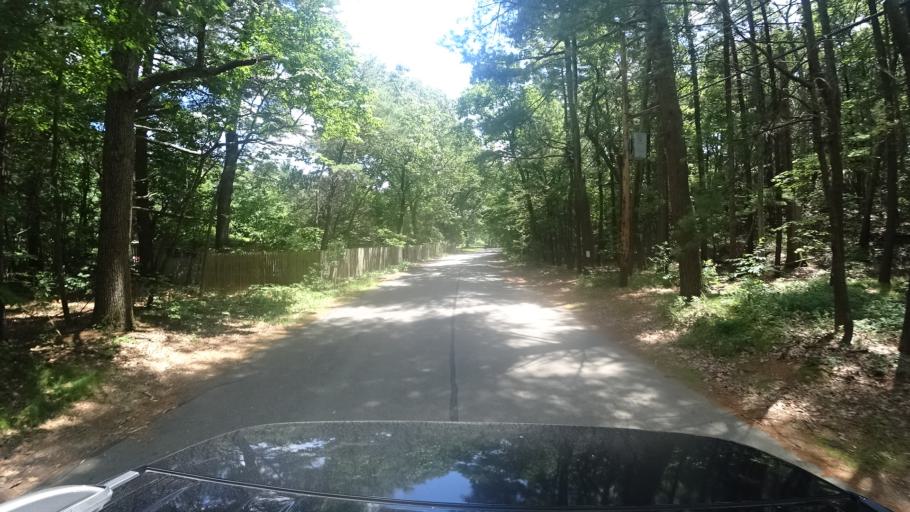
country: US
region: Massachusetts
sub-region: Norfolk County
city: Needham
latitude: 42.2637
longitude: -71.1996
